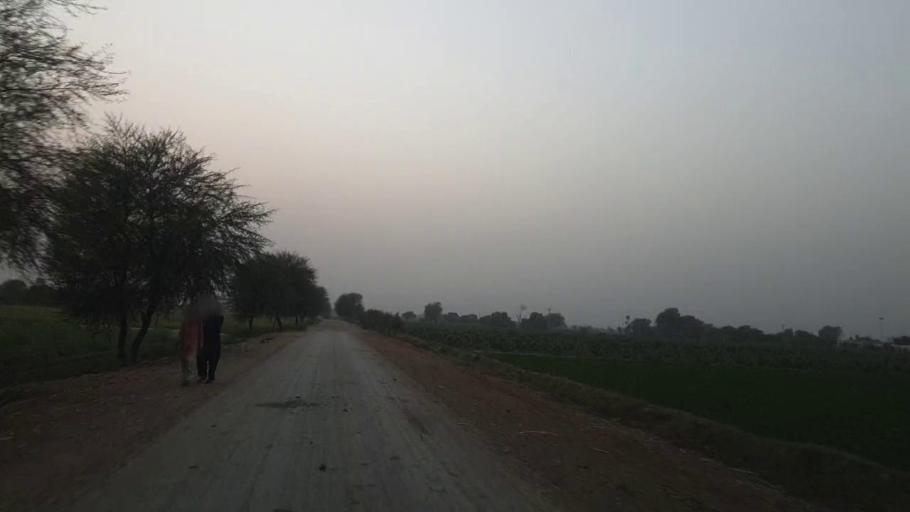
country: PK
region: Sindh
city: Kunri
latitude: 25.1134
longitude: 69.5708
